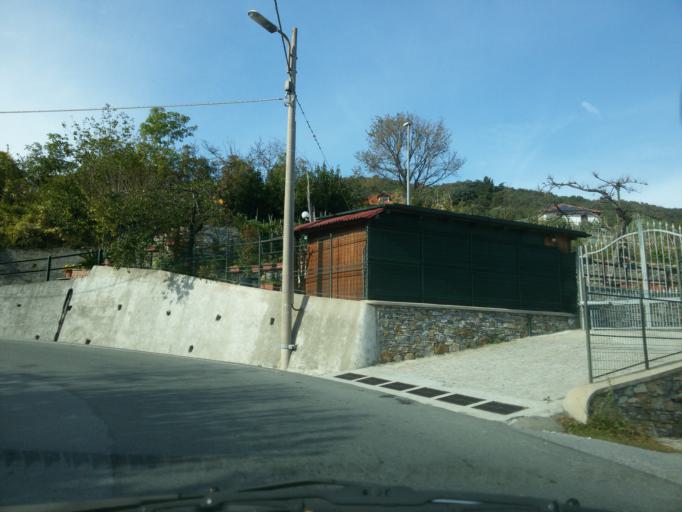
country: IT
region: Liguria
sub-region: Provincia di Genova
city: Piccarello
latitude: 44.4654
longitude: 8.9644
